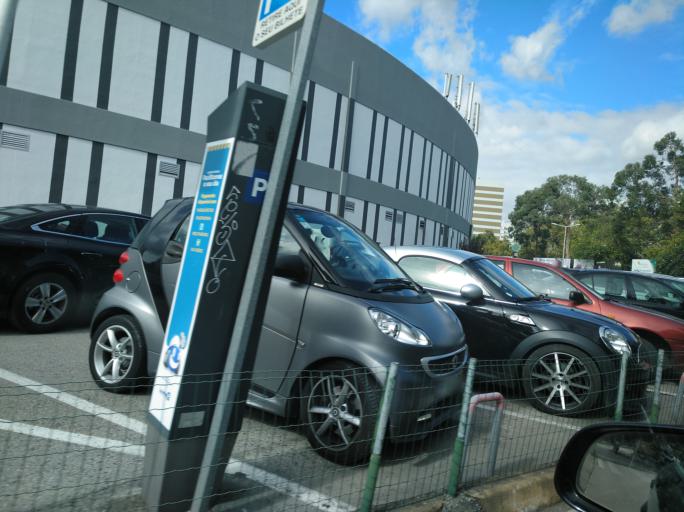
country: PT
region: Lisbon
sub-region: Loures
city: Moscavide
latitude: 38.7820
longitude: -9.1107
